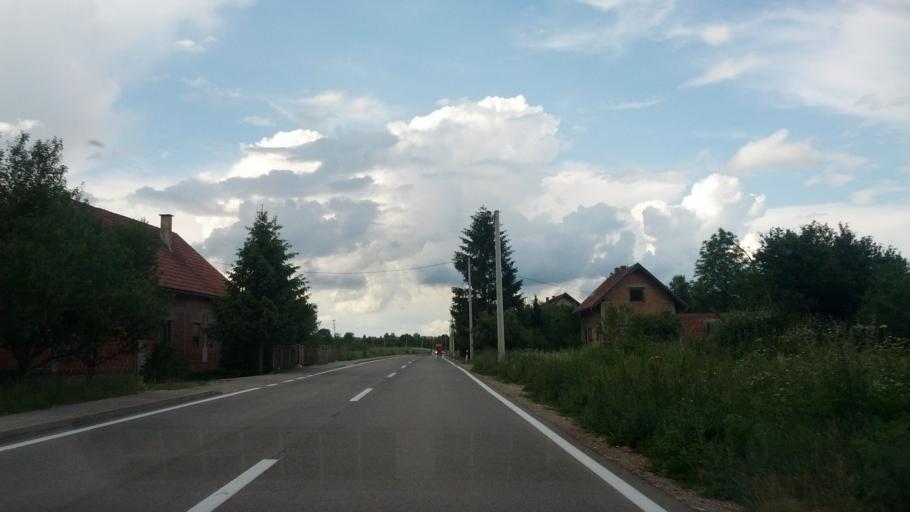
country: BA
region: Federation of Bosnia and Herzegovina
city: Izacic
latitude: 44.8976
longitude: 15.7240
